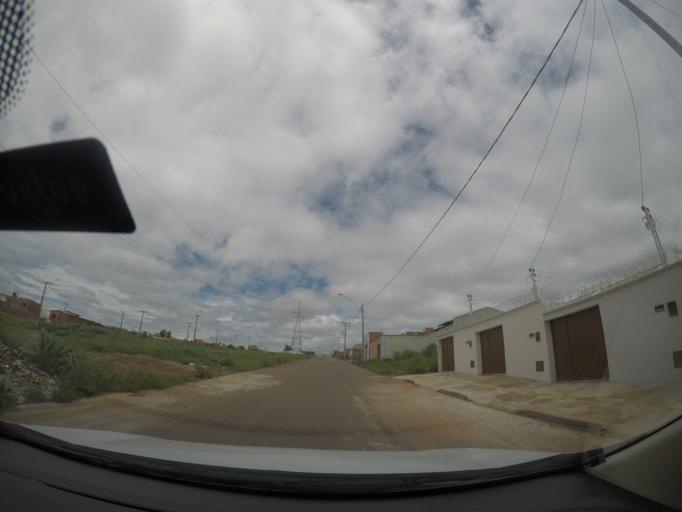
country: BR
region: Goias
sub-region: Trindade
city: Trindade
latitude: -16.7435
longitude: -49.3815
